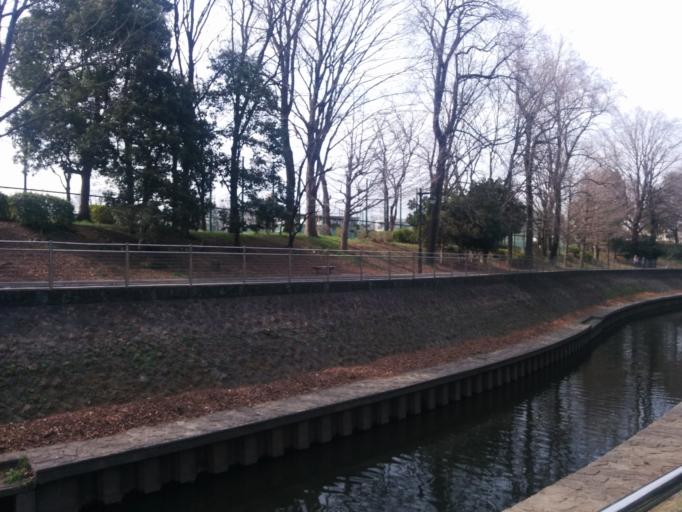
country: JP
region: Tokyo
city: Tokyo
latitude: 35.6895
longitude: 139.6327
